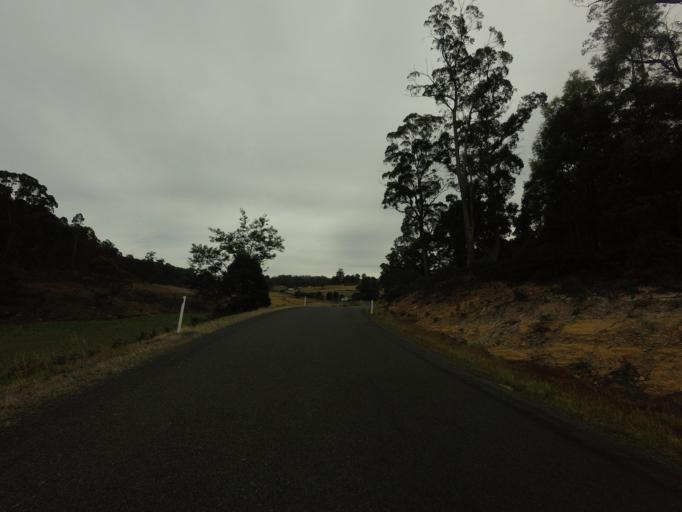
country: AU
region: Tasmania
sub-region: Sorell
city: Sorell
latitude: -42.5413
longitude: 147.5686
